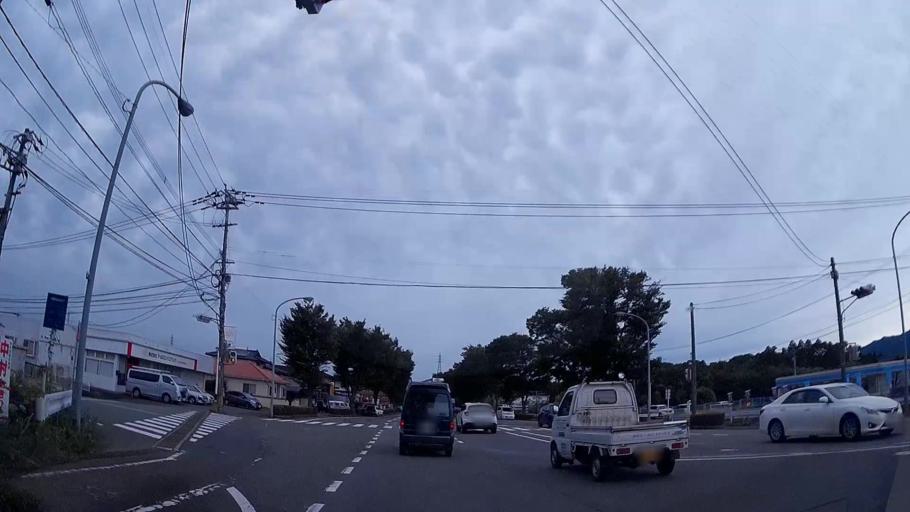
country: JP
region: Kumamoto
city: Ozu
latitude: 32.8985
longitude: 130.8532
